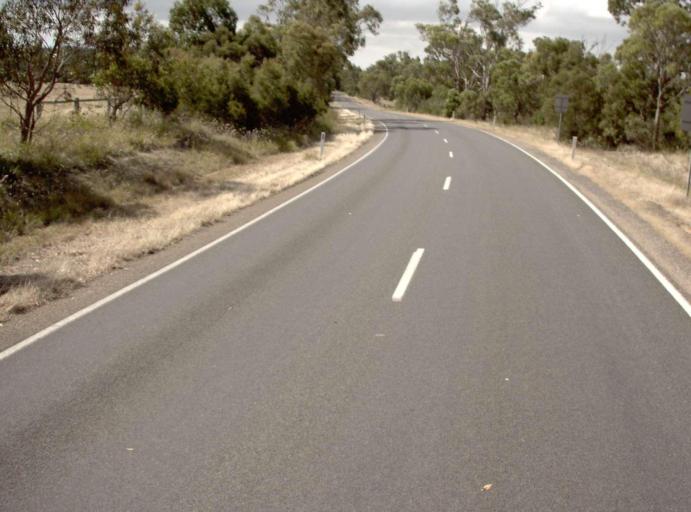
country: AU
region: Victoria
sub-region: Wellington
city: Sale
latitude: -38.2742
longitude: 147.1500
